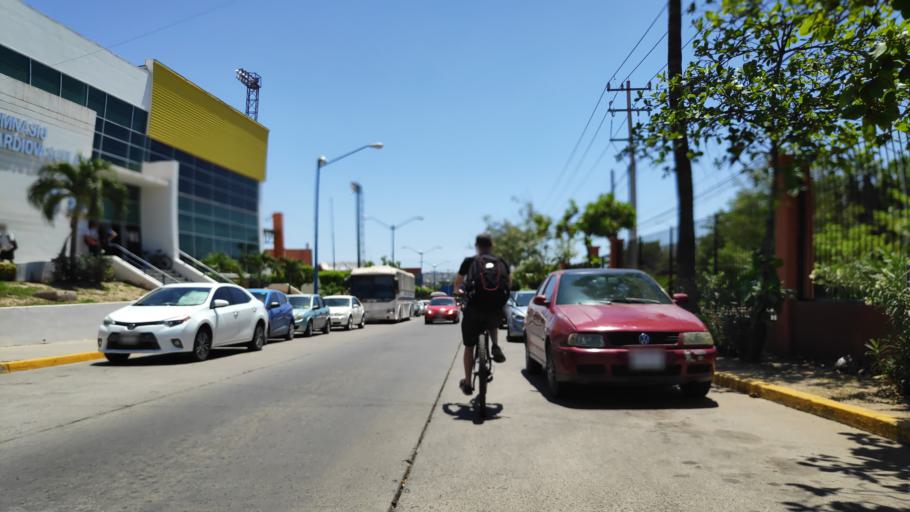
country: MX
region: Sinaloa
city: Culiacan
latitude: 24.8239
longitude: -107.3835
